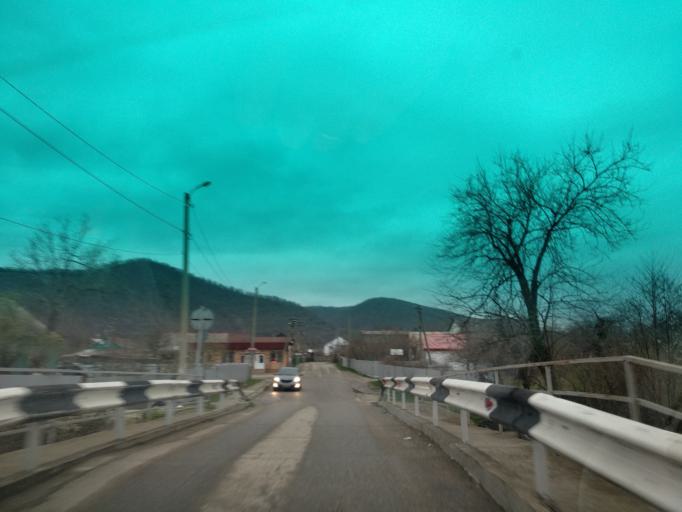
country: RU
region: Krasnodarskiy
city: Novomikhaylovskiy
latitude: 44.2594
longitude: 38.8617
